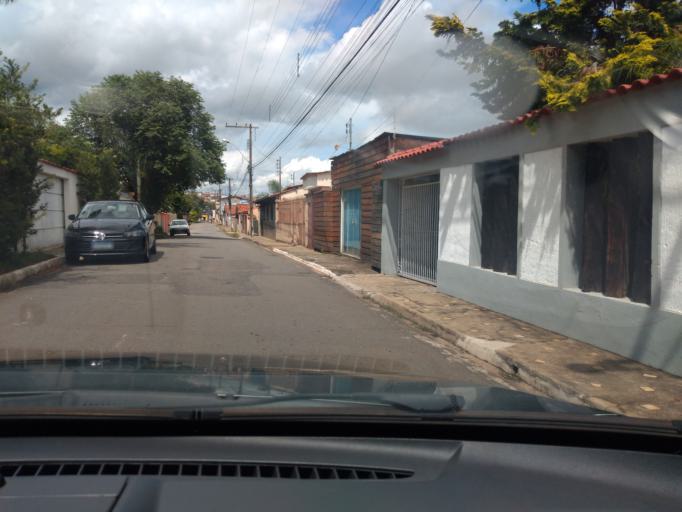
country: BR
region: Minas Gerais
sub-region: Tres Coracoes
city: Tres Coracoes
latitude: -21.6981
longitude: -45.2657
